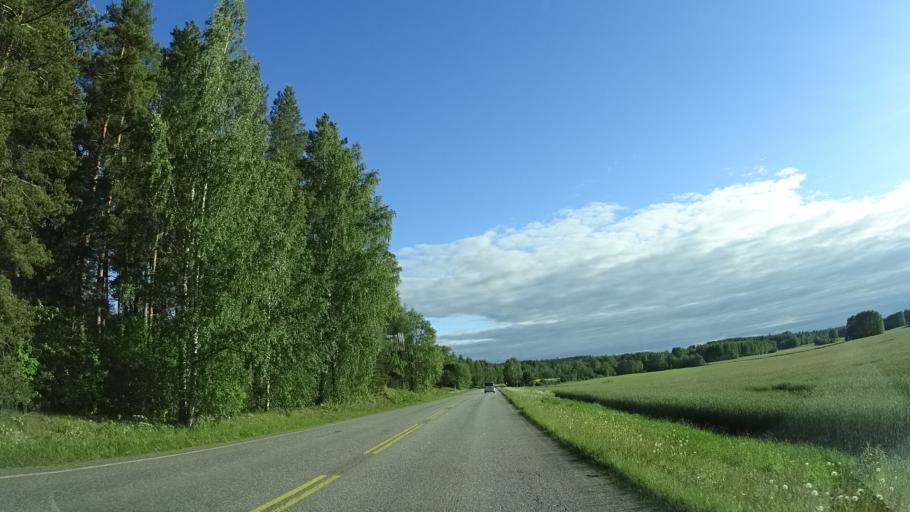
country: FI
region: Paijanne Tavastia
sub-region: Lahti
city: Sysmae
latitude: 61.3509
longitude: 25.6185
